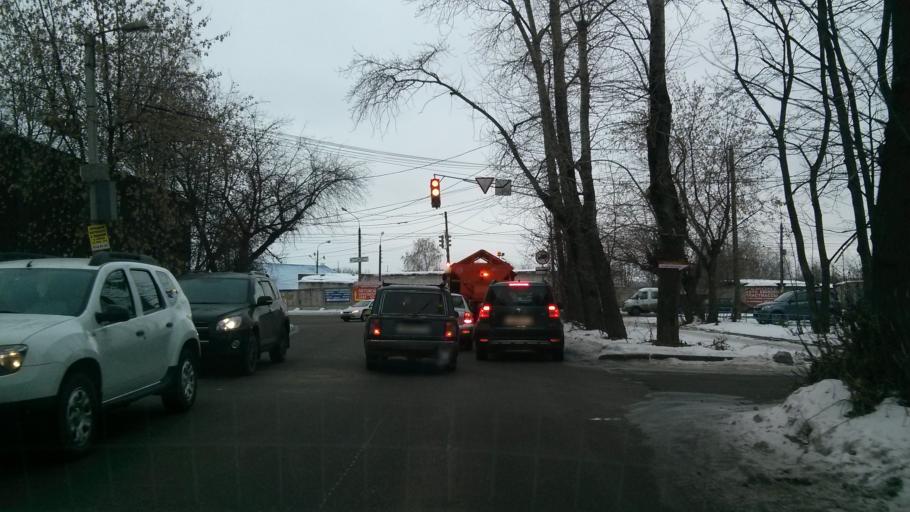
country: RU
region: Nizjnij Novgorod
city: Nizhniy Novgorod
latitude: 56.3100
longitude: 44.0056
